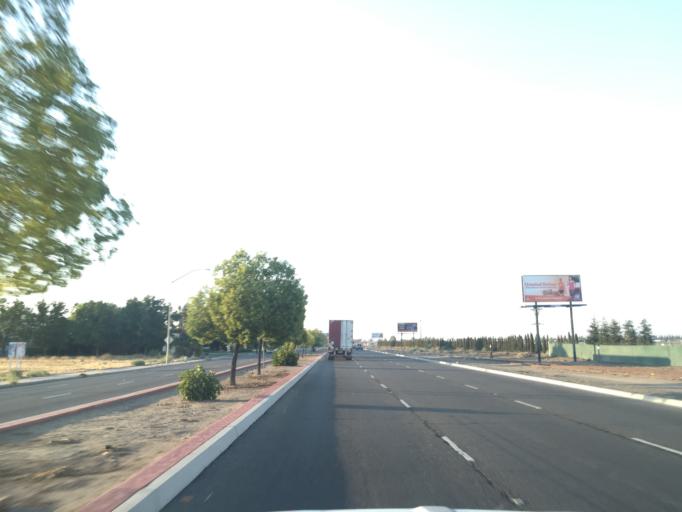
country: US
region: California
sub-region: Fresno County
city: Sunnyside
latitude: 36.7585
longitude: -119.7004
